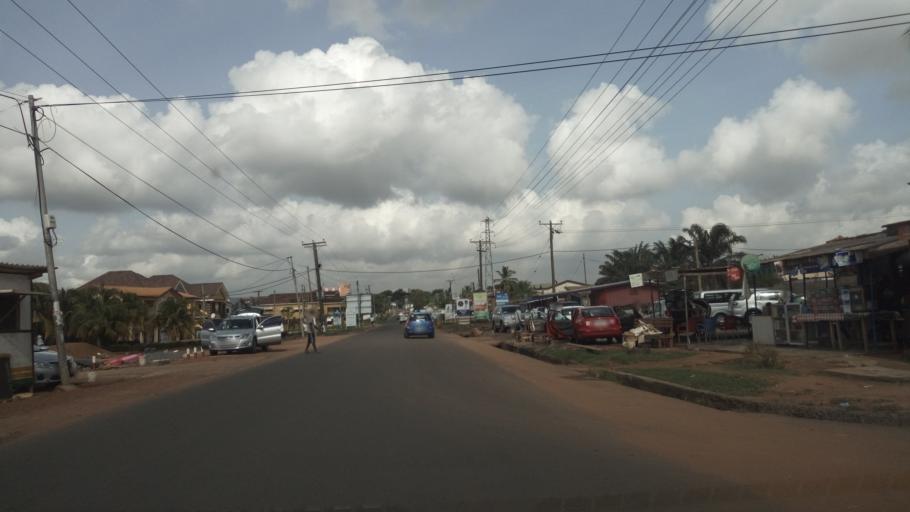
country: GH
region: Greater Accra
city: Medina Estates
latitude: 5.6599
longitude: -0.1558
